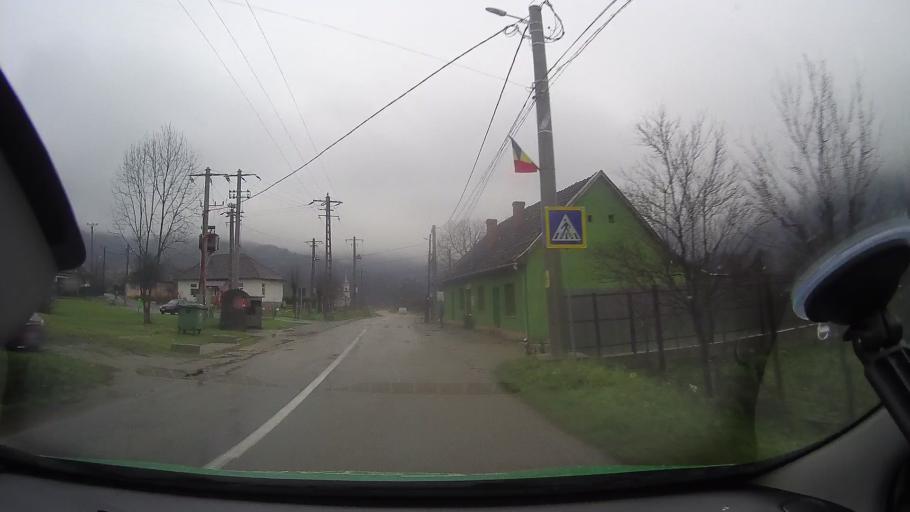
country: RO
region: Arad
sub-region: Comuna Moneasa
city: Moneasa
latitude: 46.4258
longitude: 22.2545
